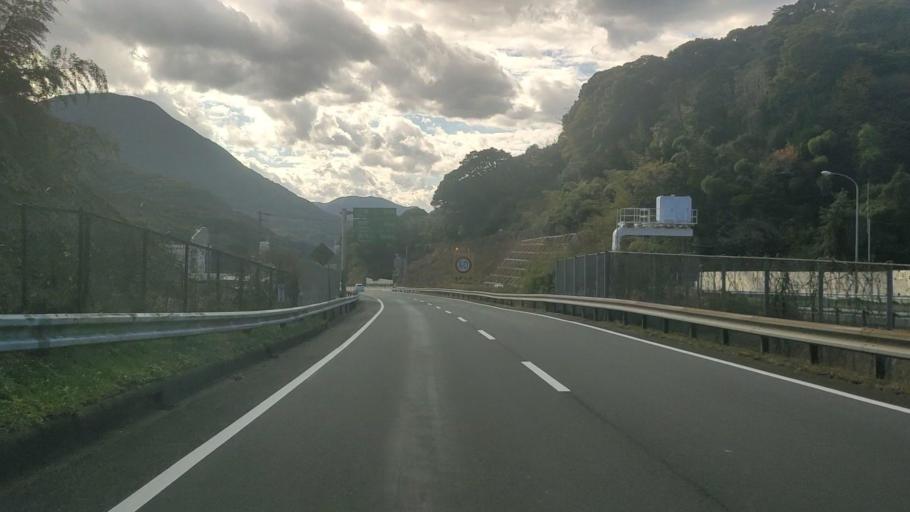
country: JP
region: Yamaguchi
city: Shimonoseki
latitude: 33.9161
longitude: 130.9626
